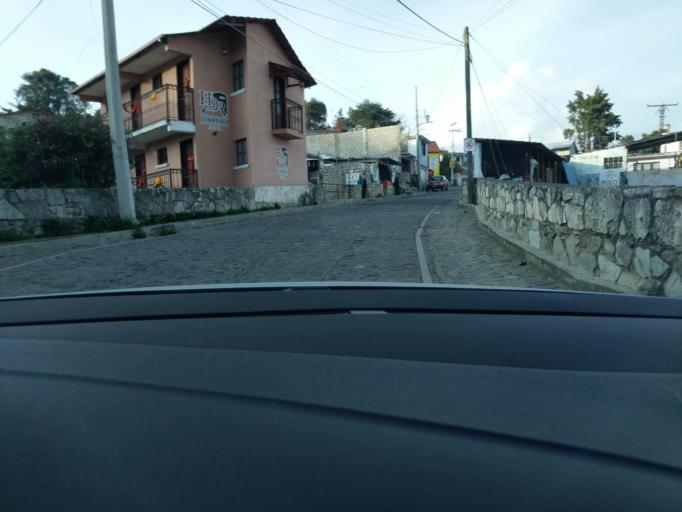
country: MX
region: Hidalgo
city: Mineral del Monte
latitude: 20.1419
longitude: -98.6734
